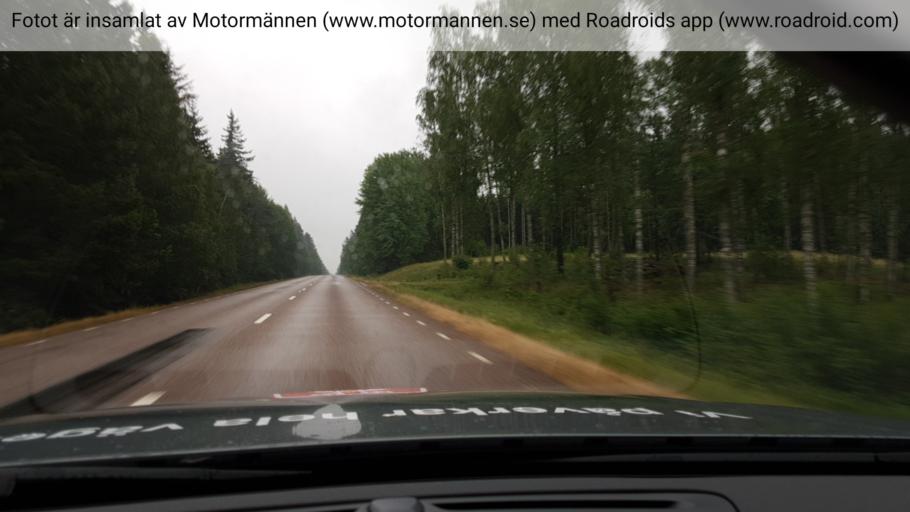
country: SE
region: Dalarna
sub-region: Avesta Kommun
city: Avesta
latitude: 59.9726
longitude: 16.1541
